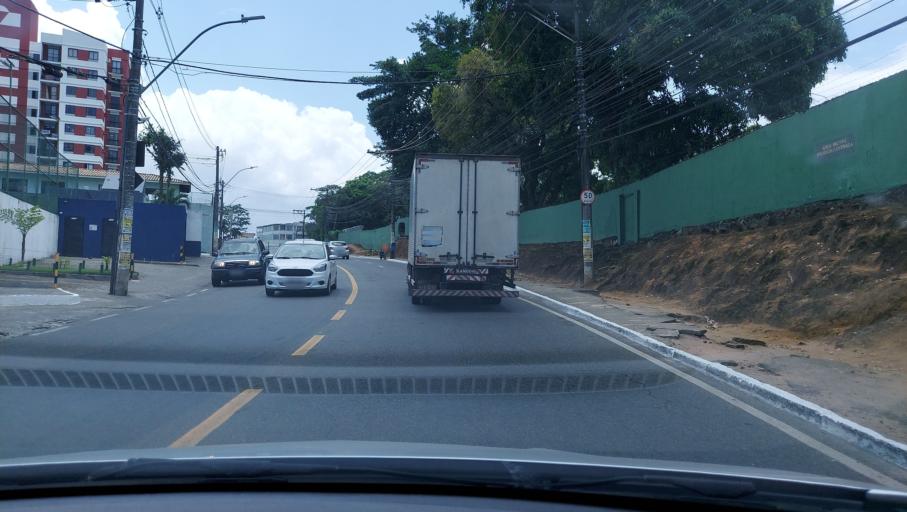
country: BR
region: Bahia
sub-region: Salvador
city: Salvador
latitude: -12.9563
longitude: -38.4643
